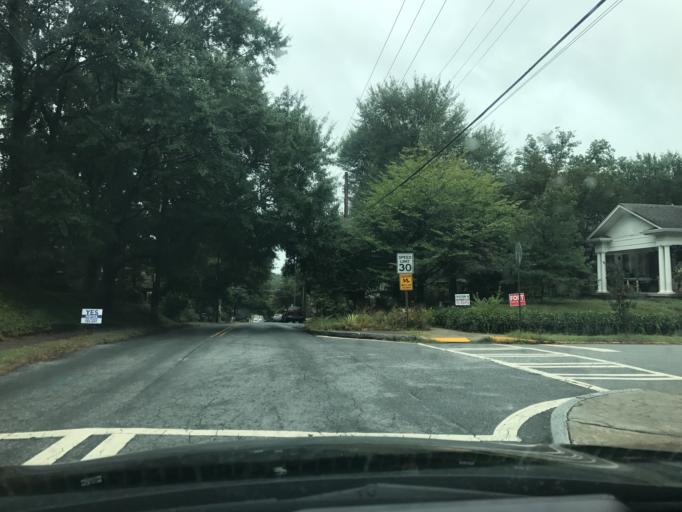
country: US
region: Georgia
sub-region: DeKalb County
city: Druid Hills
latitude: 33.7650
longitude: -84.3471
